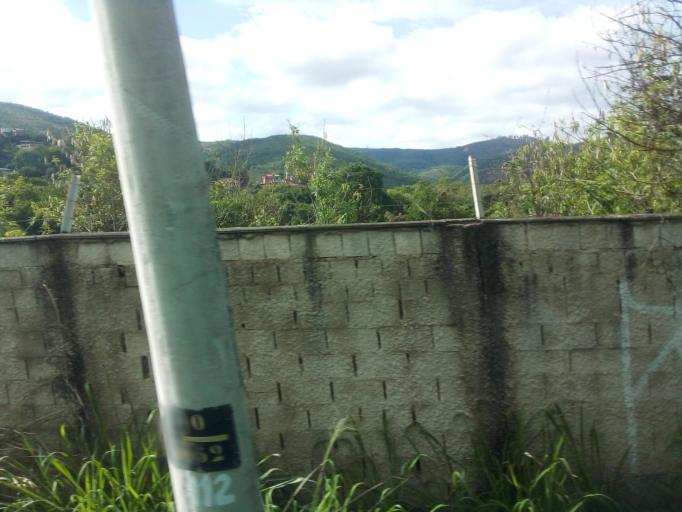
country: BR
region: Minas Gerais
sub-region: Belo Horizonte
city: Belo Horizonte
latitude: -19.8842
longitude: -43.8633
